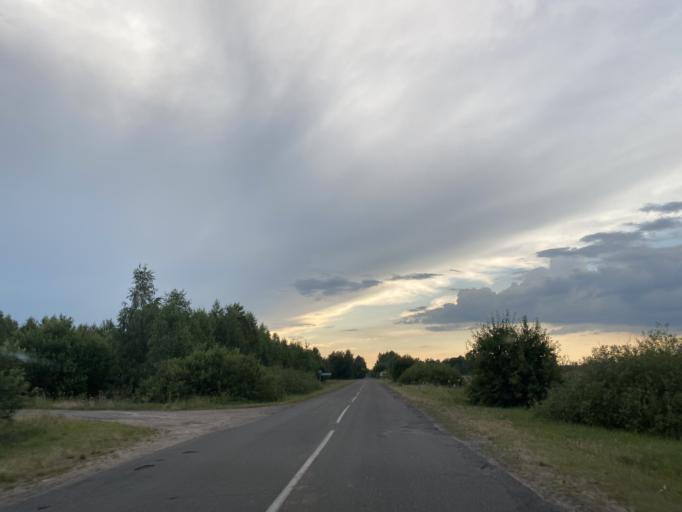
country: BY
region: Brest
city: Ivanava
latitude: 52.3395
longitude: 25.6233
